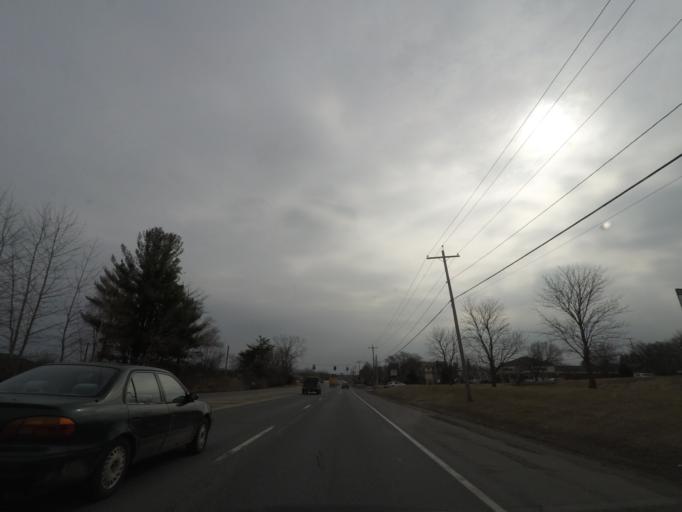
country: US
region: New York
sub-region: Warren County
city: Glens Falls
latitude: 43.3320
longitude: -73.6561
